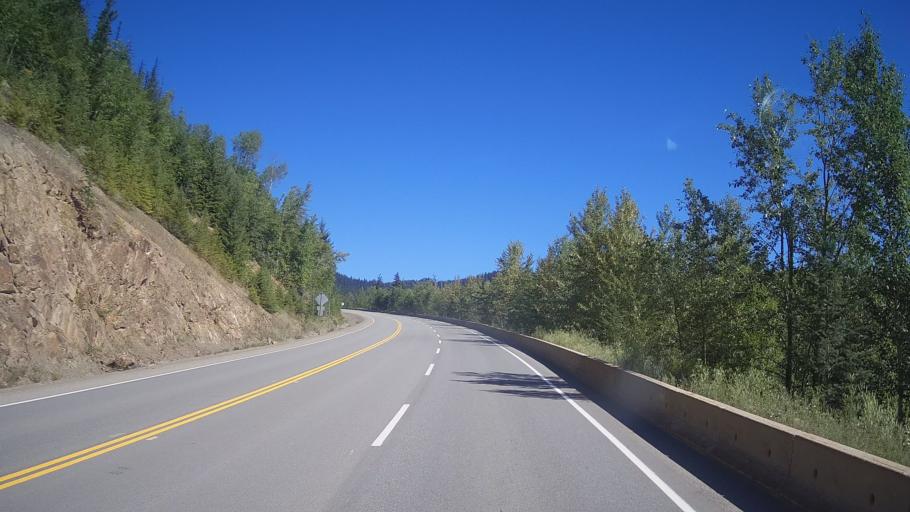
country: CA
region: British Columbia
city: Kamloops
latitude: 51.4906
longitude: -120.2690
